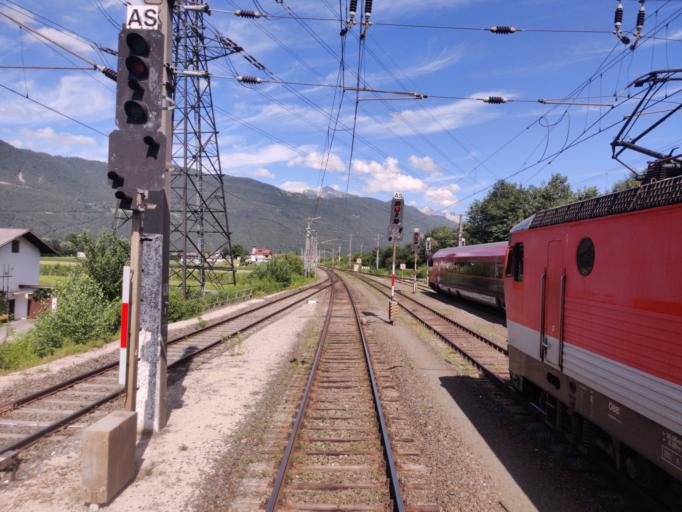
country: AT
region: Tyrol
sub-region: Politischer Bezirk Innsbruck Land
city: Pfaffenhofen
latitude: 47.3009
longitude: 11.0826
